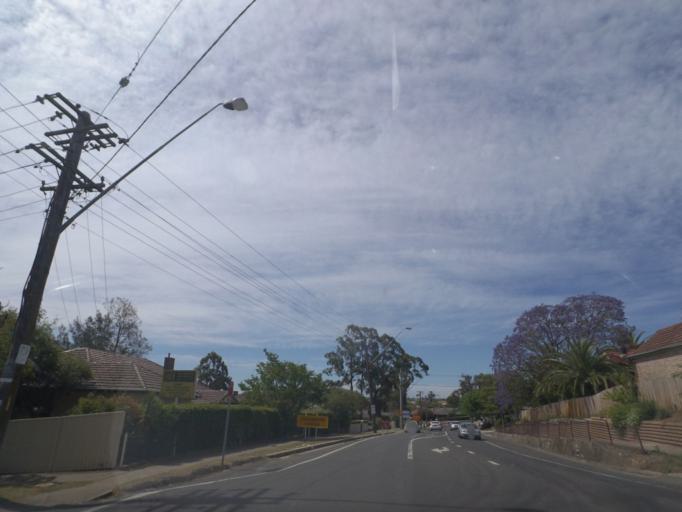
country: AU
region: New South Wales
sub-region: Camden
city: Elderslie
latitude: -34.0587
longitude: 150.6938
